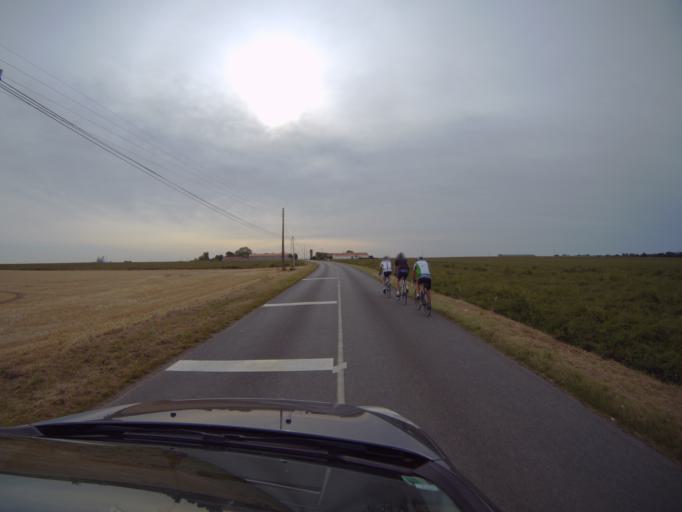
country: FR
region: Pays de la Loire
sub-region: Departement de la Vendee
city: Angles
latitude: 46.4072
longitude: -1.4358
